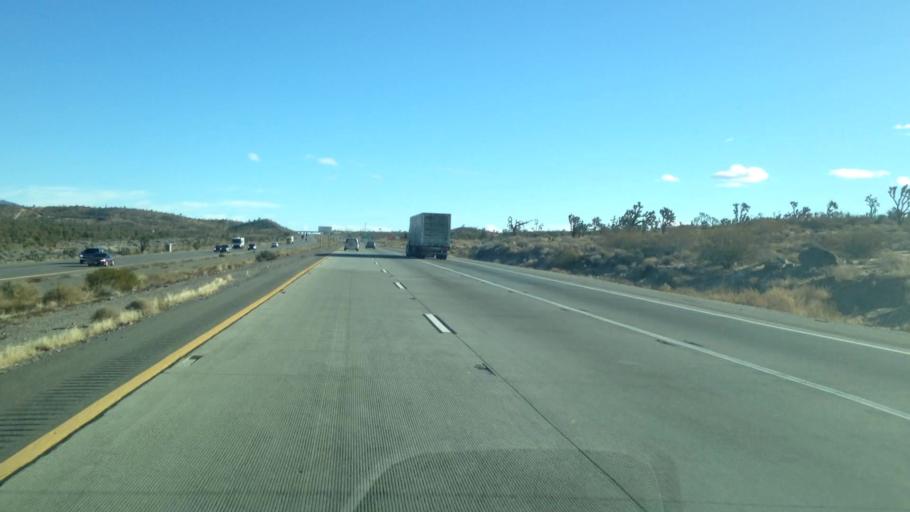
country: US
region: Nevada
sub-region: Clark County
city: Sandy Valley
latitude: 35.3959
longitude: -115.8179
